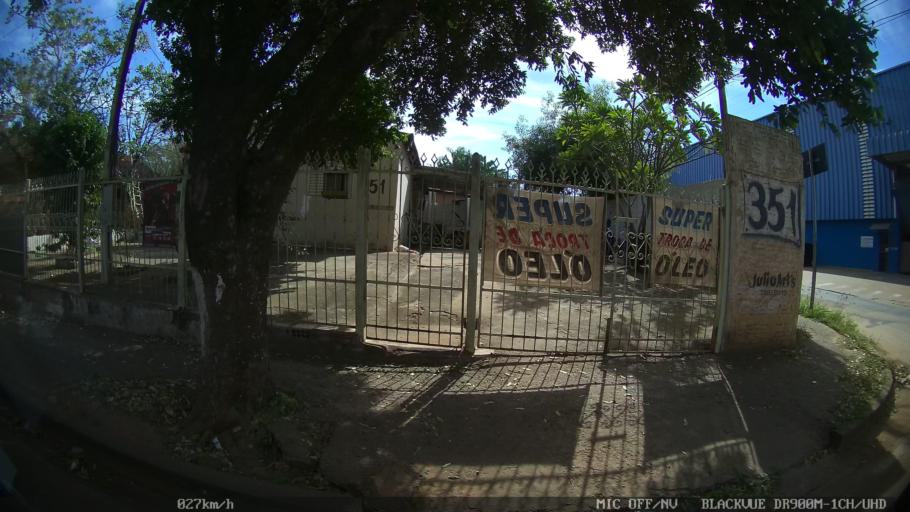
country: BR
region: Sao Paulo
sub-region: Sao Jose Do Rio Preto
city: Sao Jose do Rio Preto
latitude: -20.8413
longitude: -49.3337
